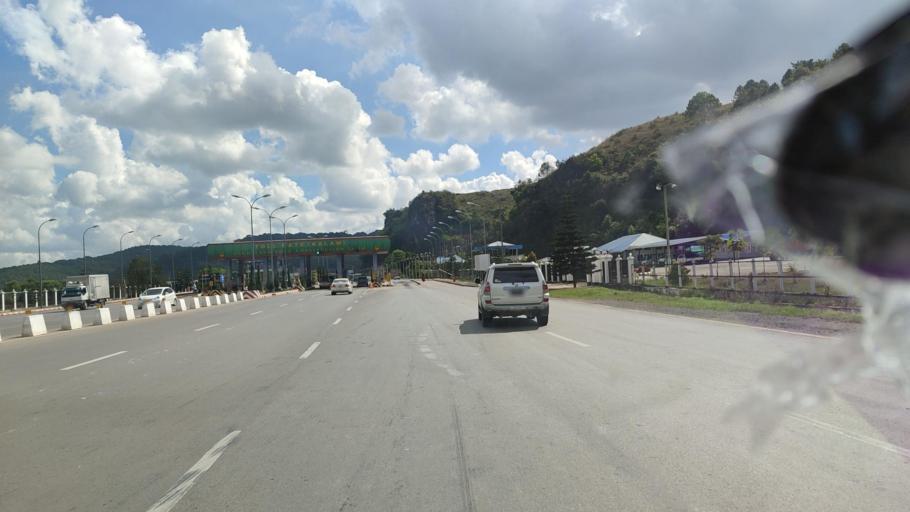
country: MM
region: Shan
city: Taunggyi
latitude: 20.6460
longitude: 96.6016
